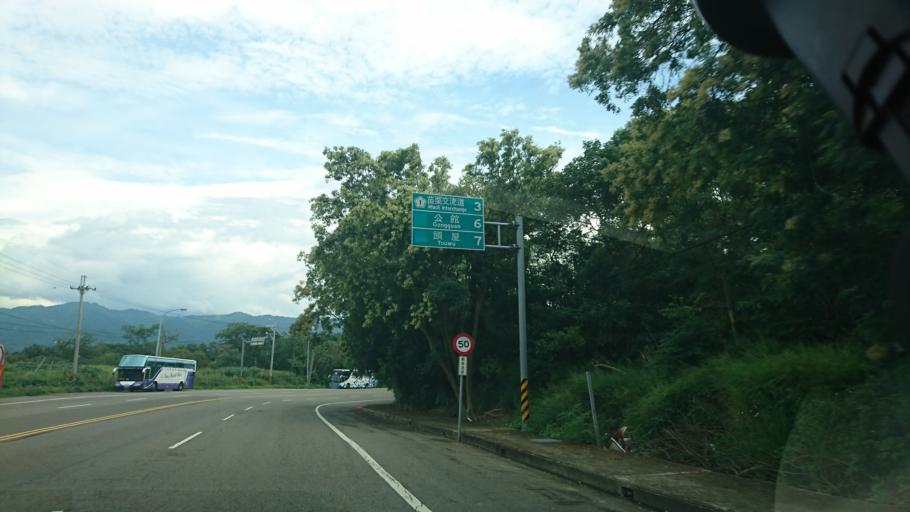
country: TW
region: Taiwan
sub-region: Miaoli
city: Miaoli
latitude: 24.5429
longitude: 120.8108
